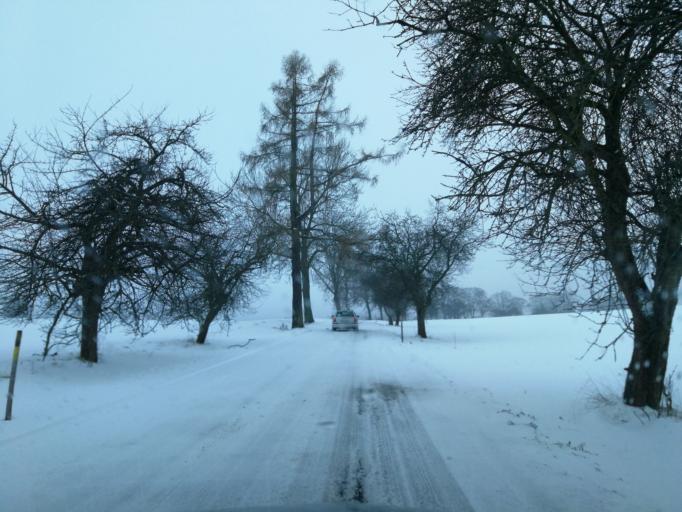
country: CZ
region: Vysocina
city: Heralec
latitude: 49.5331
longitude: 15.4283
